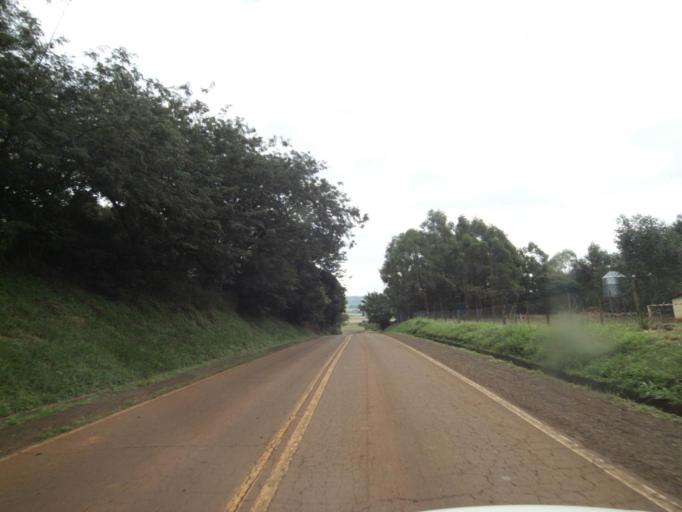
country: BR
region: Parana
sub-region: Marechal Candido Rondon
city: Marechal Candido Rondon
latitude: -24.7940
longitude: -54.2243
